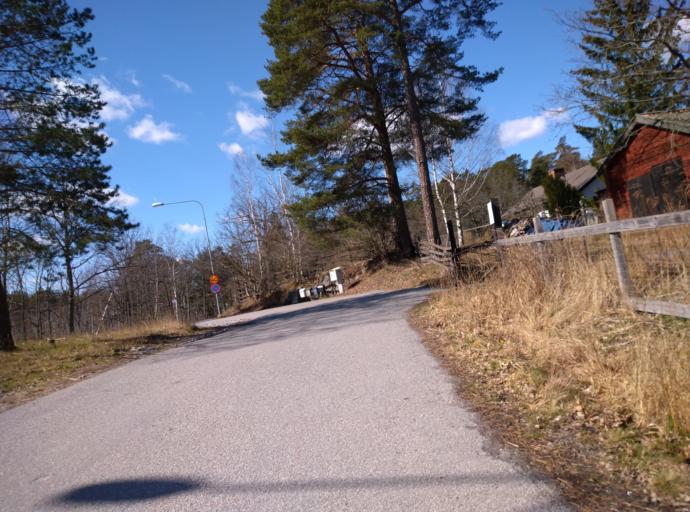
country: SE
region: Stockholm
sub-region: Nacka Kommun
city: Fisksatra
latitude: 59.2944
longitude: 18.2365
